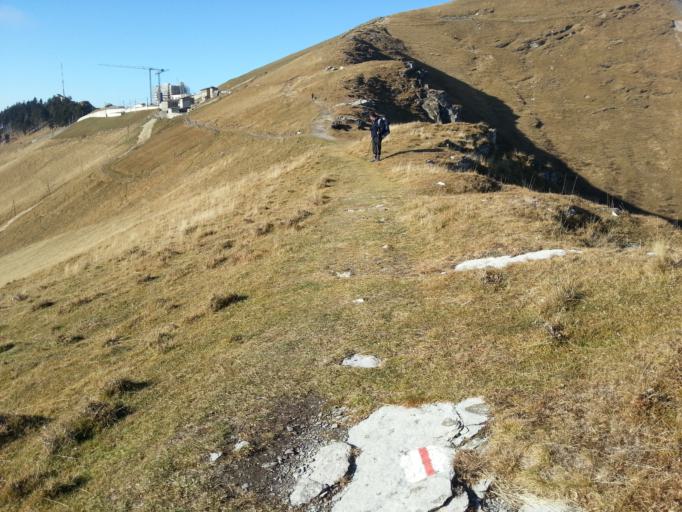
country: CH
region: Ticino
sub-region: Lugano District
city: Melano
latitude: 45.9288
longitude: 9.0253
